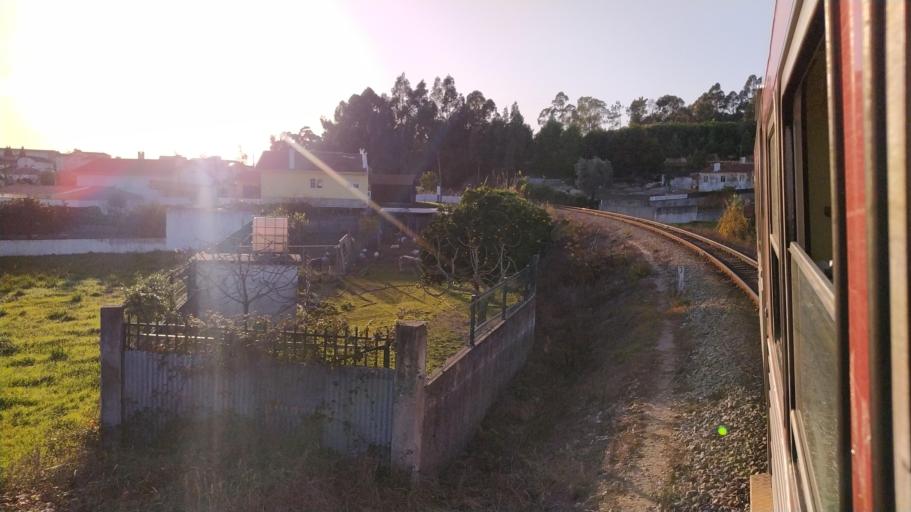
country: PT
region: Aveiro
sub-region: Aveiro
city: Eixo
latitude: 40.6401
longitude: -8.5929
